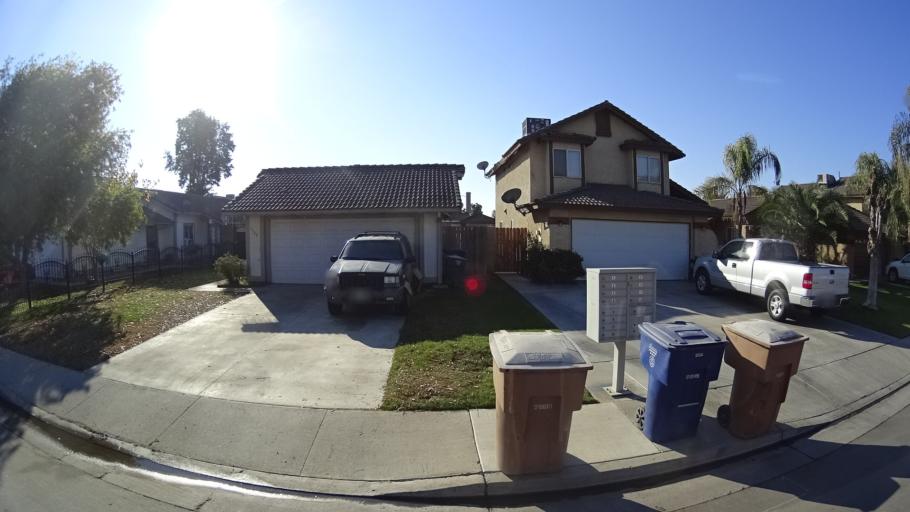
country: US
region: California
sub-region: Kern County
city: Greenfield
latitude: 35.3053
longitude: -119.0197
